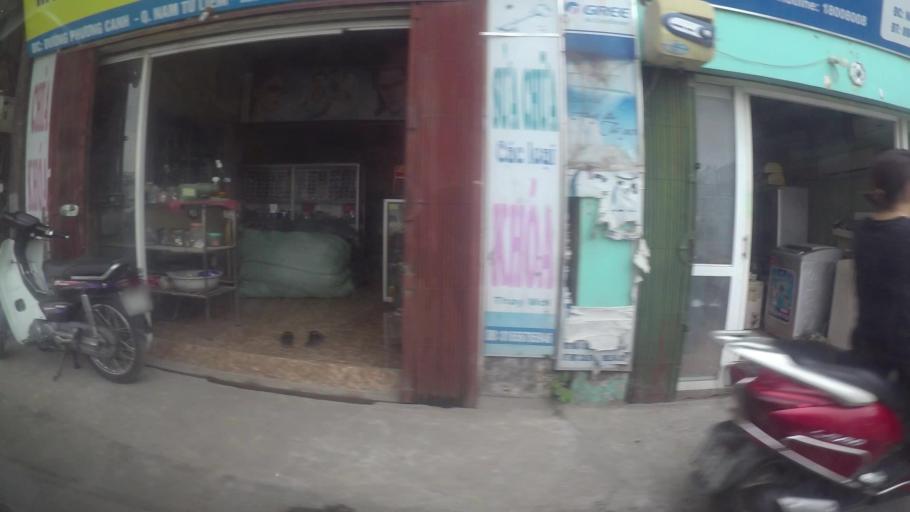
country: VN
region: Ha Noi
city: Cau Dien
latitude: 21.0343
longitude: 105.7447
